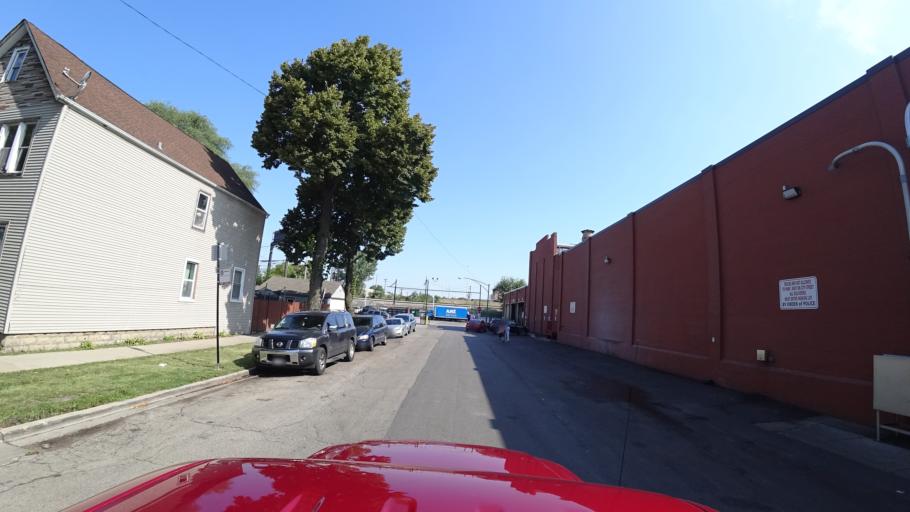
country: US
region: Illinois
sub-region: Cook County
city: Cicero
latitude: 41.8253
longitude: -87.7069
